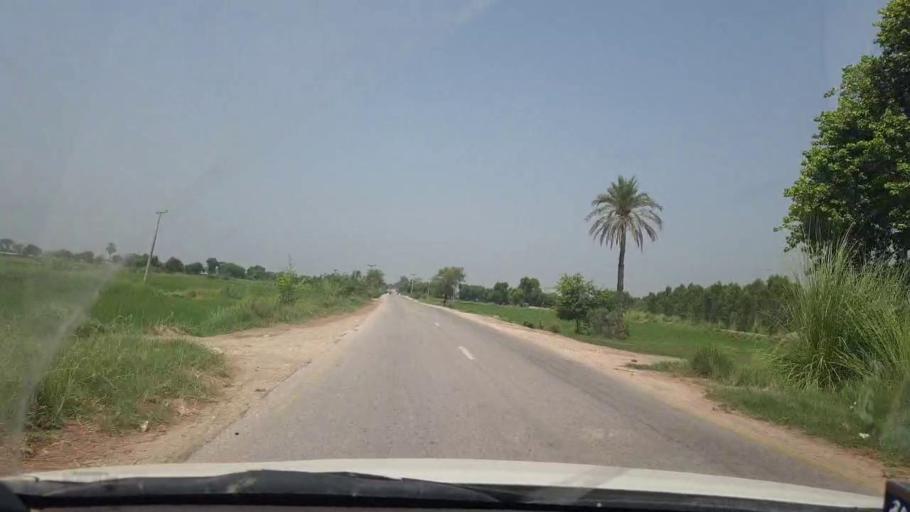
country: PK
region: Sindh
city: Shikarpur
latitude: 27.9542
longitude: 68.6730
